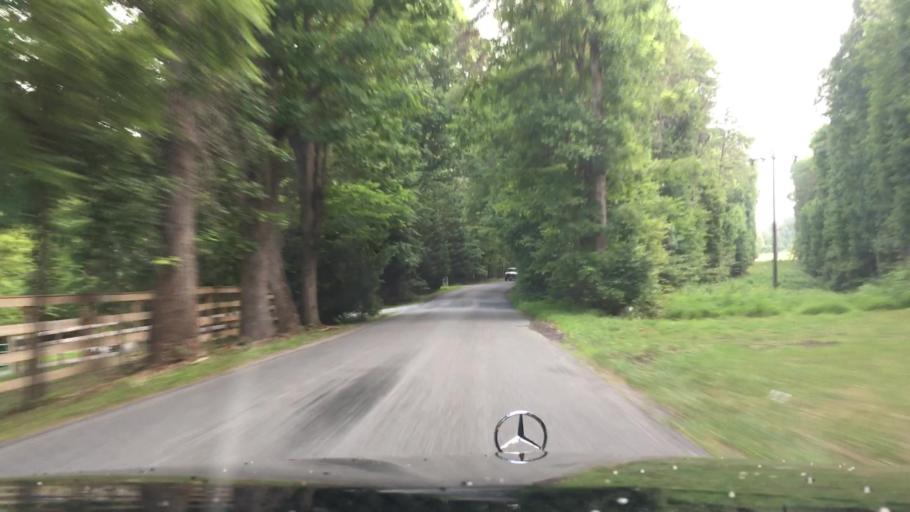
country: US
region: Virginia
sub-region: Campbell County
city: Timberlake
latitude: 37.2665
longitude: -79.3122
